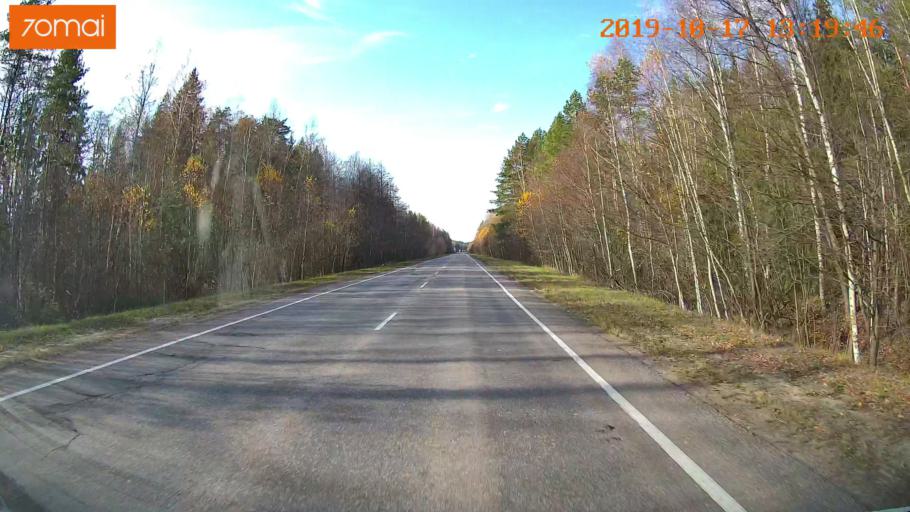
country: RU
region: Rjazan
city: Gus'-Zheleznyy
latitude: 55.0716
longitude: 41.0661
